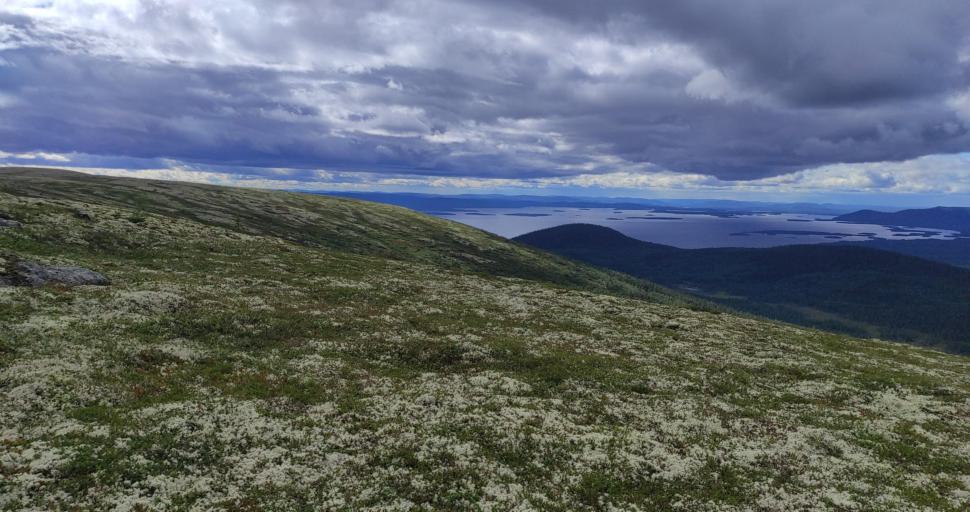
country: RU
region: Murmansk
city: Afrikanda
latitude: 67.0510
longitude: 32.9614
